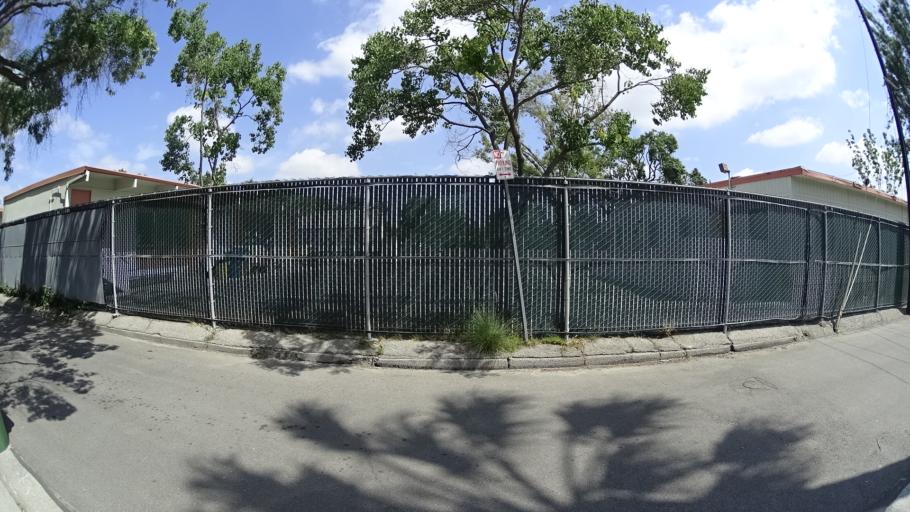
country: US
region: California
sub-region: Los Angeles County
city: Universal City
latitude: 34.1585
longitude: -118.3599
